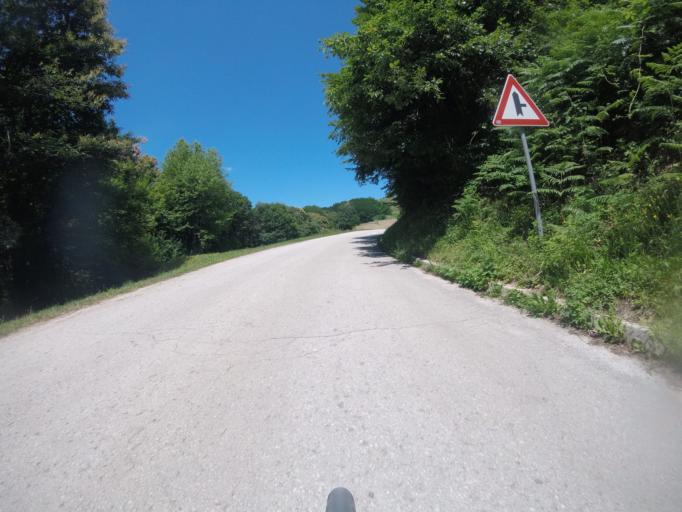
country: HR
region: Karlovacka
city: Ozalj
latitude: 45.6773
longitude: 15.4395
